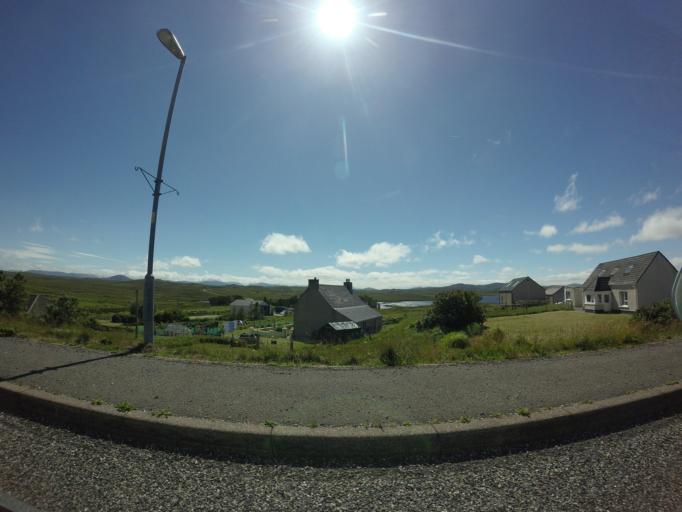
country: GB
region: Scotland
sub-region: Eilean Siar
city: Harris
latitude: 58.1882
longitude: -6.7044
